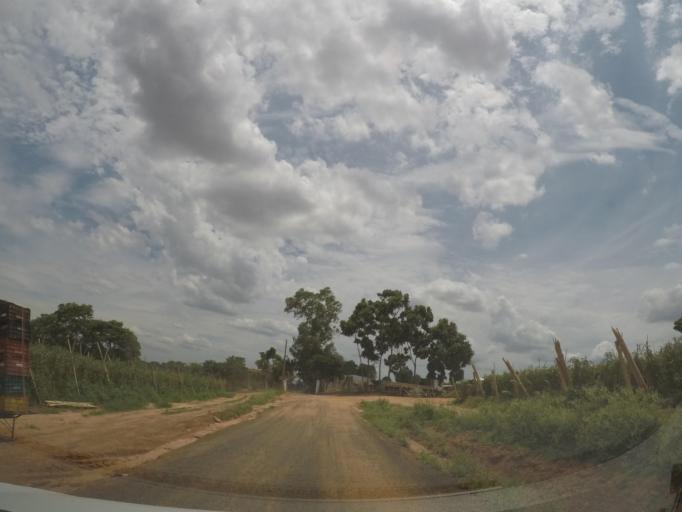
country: BR
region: Sao Paulo
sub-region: Sumare
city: Sumare
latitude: -22.8379
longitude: -47.2843
